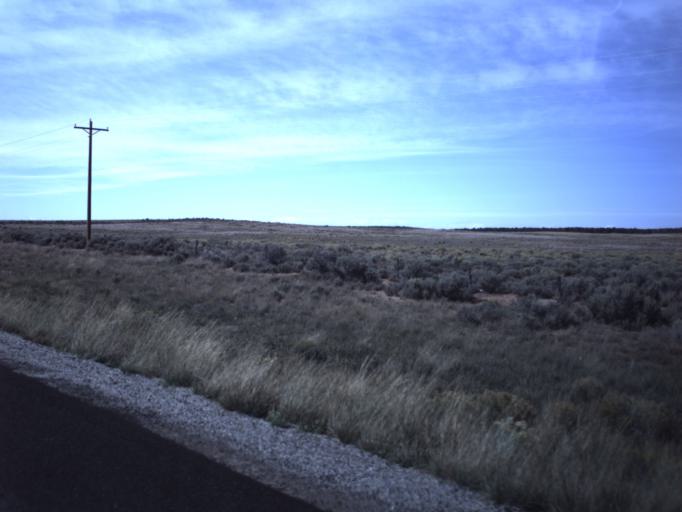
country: US
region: Utah
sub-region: San Juan County
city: Monticello
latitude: 37.8509
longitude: -109.1678
